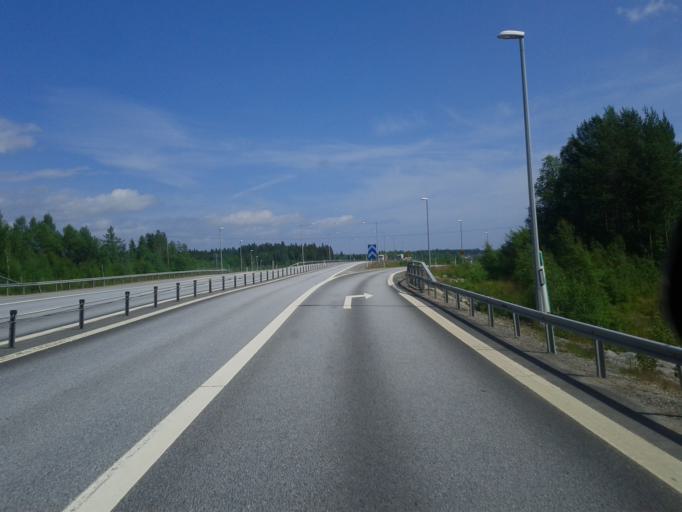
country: SE
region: Vaesterbotten
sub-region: Nordmalings Kommun
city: Nordmaling
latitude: 63.5767
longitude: 19.4560
